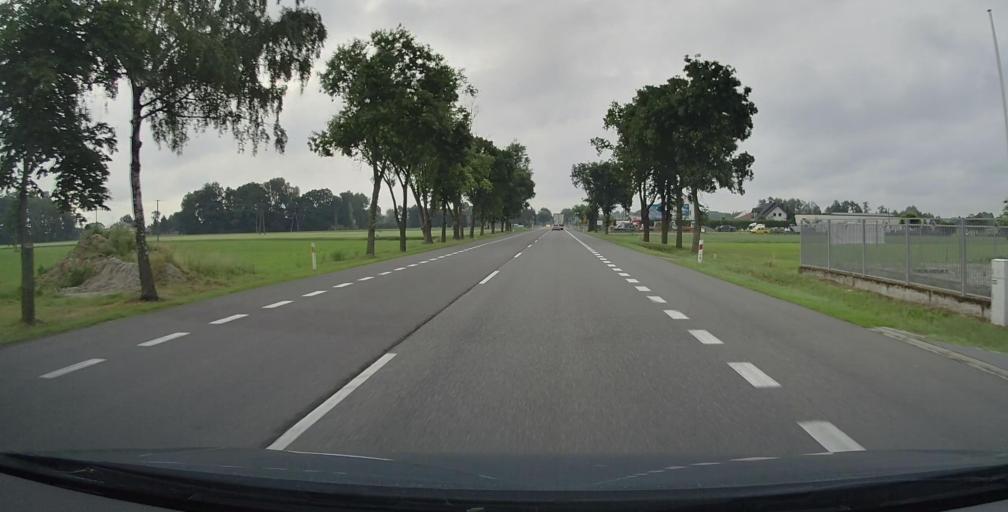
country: PL
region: Masovian Voivodeship
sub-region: Powiat siedlecki
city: Zbuczyn
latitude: 52.0743
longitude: 22.5005
